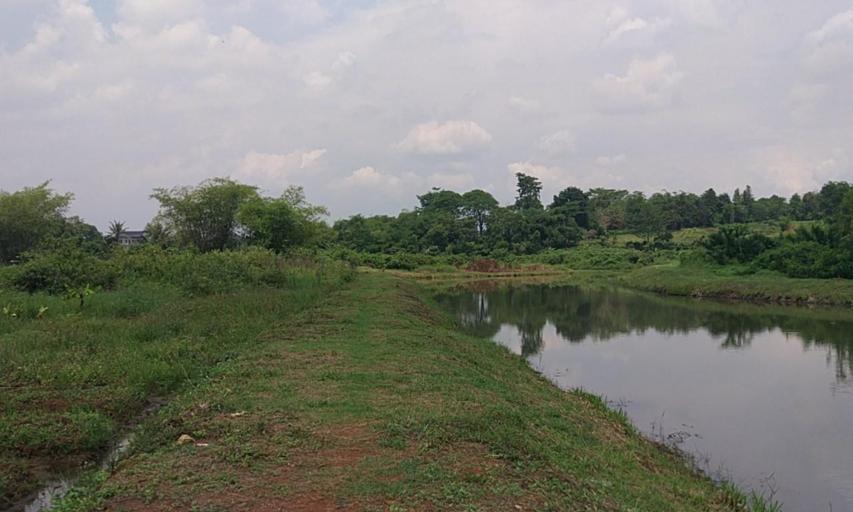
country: ID
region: West Java
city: Parung
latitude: -6.4750
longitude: 106.7759
